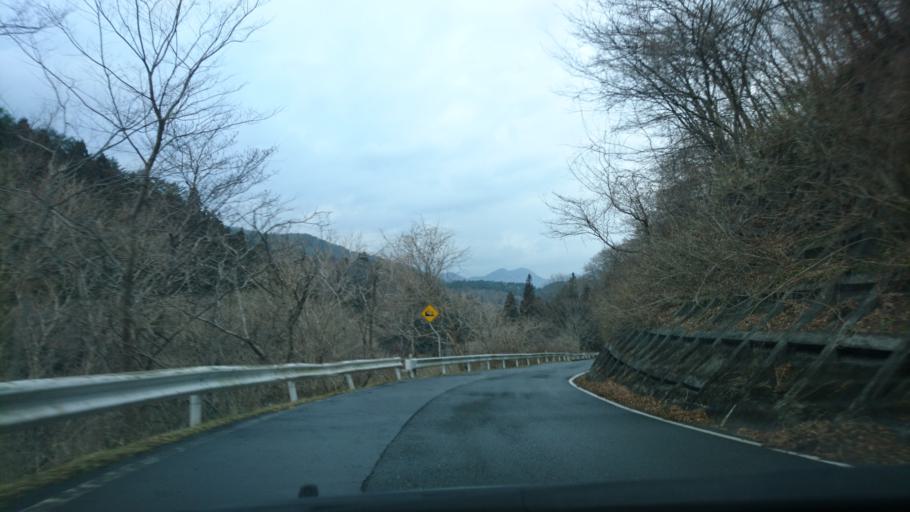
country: JP
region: Iwate
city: Ofunato
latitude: 39.0017
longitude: 141.5459
